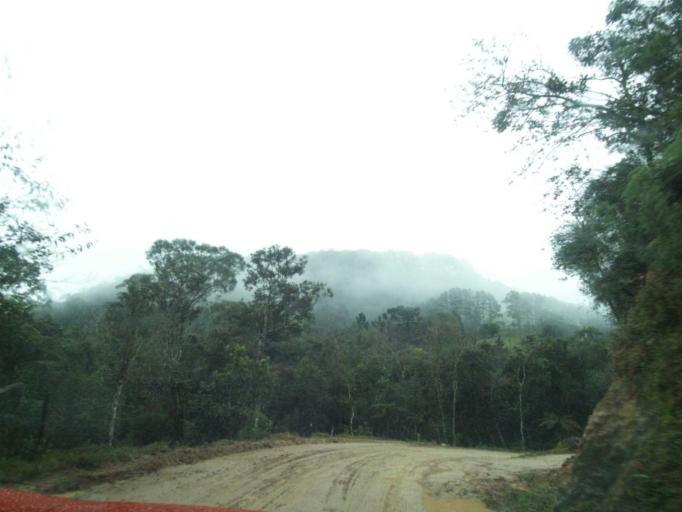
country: BR
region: Santa Catarina
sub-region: Anitapolis
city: Anitapolis
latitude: -27.9009
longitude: -49.1952
